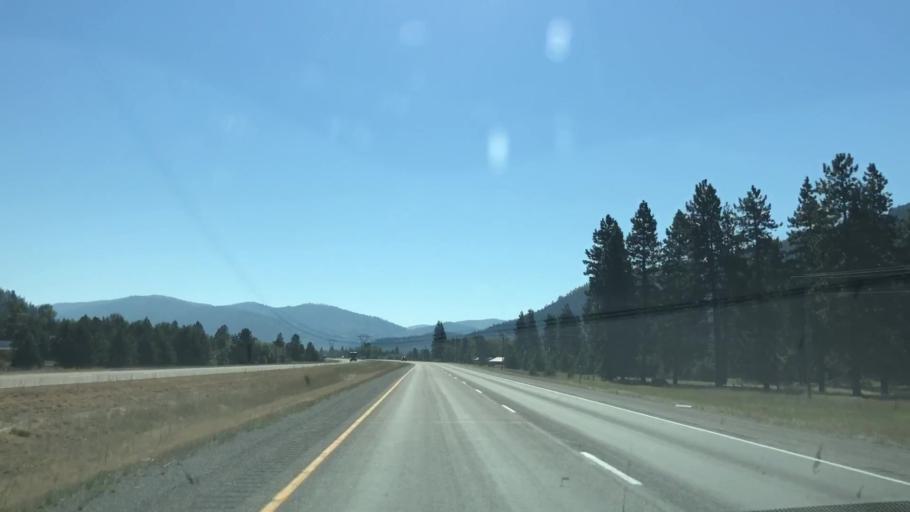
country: US
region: Montana
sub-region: Missoula County
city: Clinton
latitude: 46.8049
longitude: -113.7712
